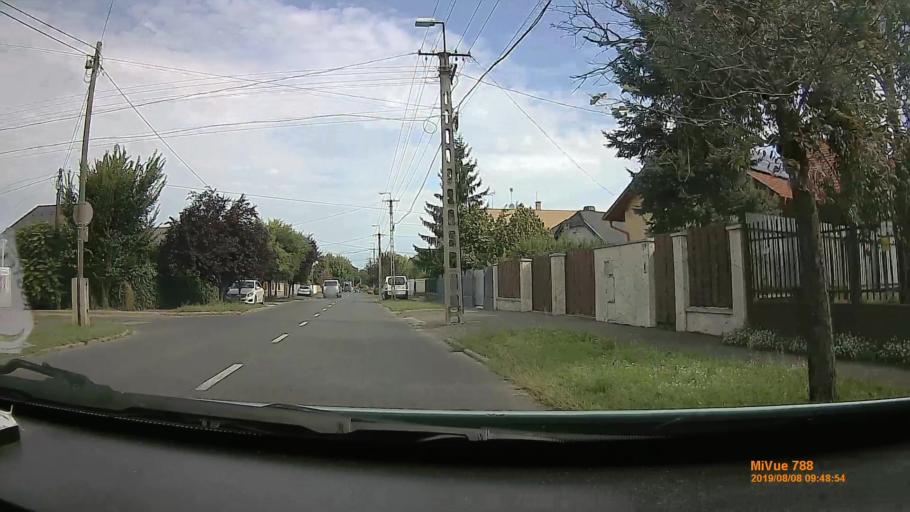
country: HU
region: Hajdu-Bihar
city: Debrecen
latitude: 47.5435
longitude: 21.6536
